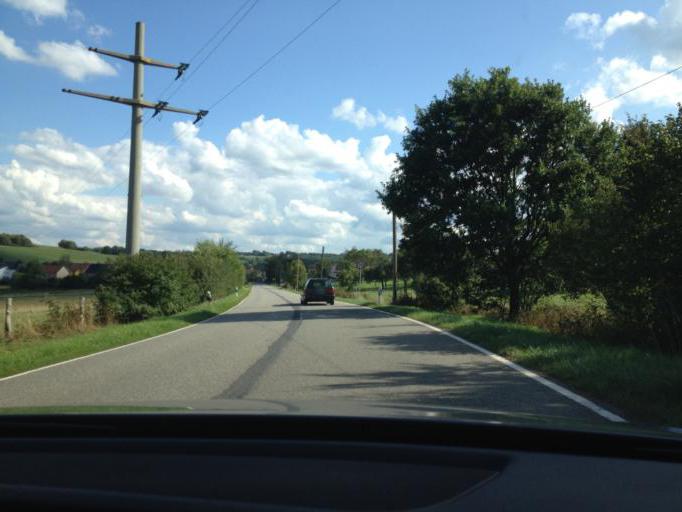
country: DE
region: Saarland
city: Illingen
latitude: 49.4059
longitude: 7.0760
